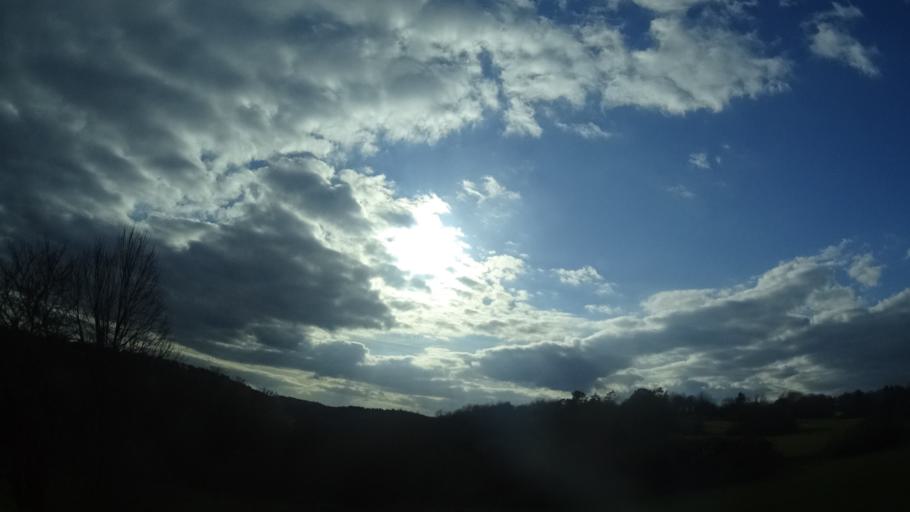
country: DE
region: Rheinland-Pfalz
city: Kronweiler
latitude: 49.6469
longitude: 7.2750
